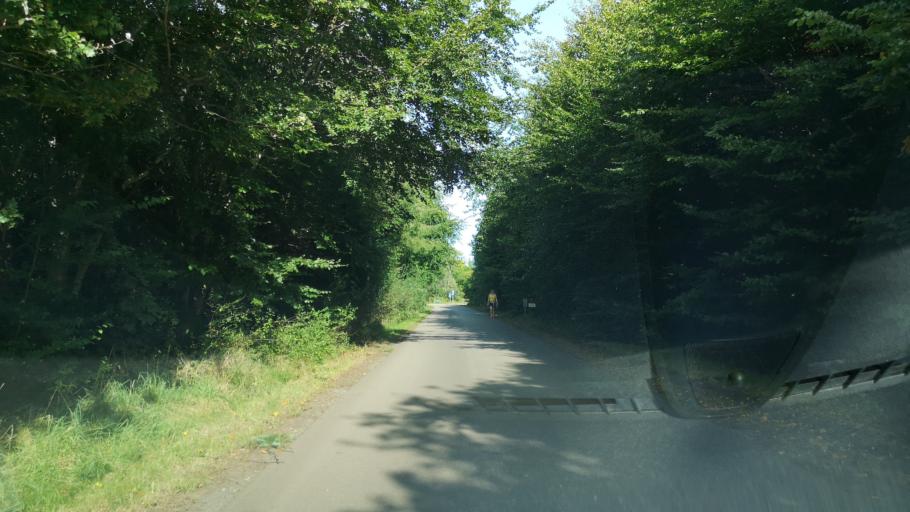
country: DK
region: Central Jutland
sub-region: Herning Kommune
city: Herning
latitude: 56.1748
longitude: 8.9586
